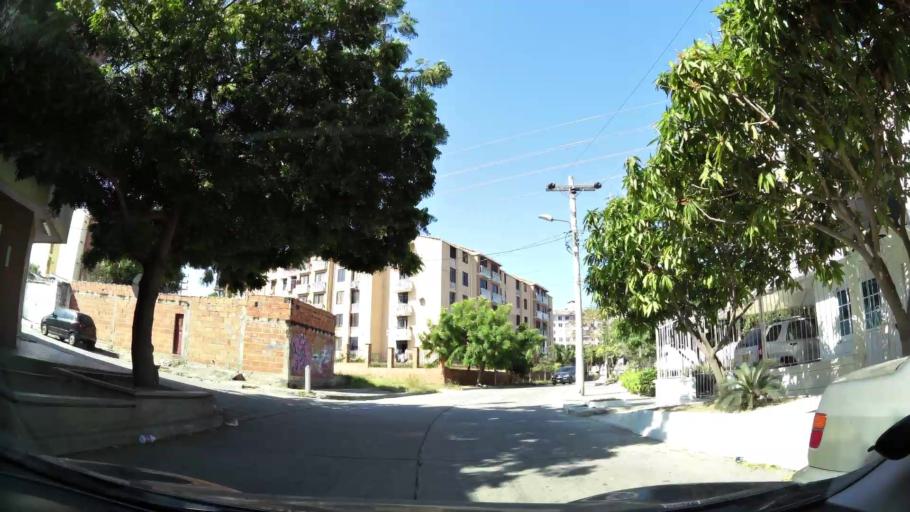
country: CO
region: Atlantico
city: Barranquilla
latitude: 11.0232
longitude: -74.8109
